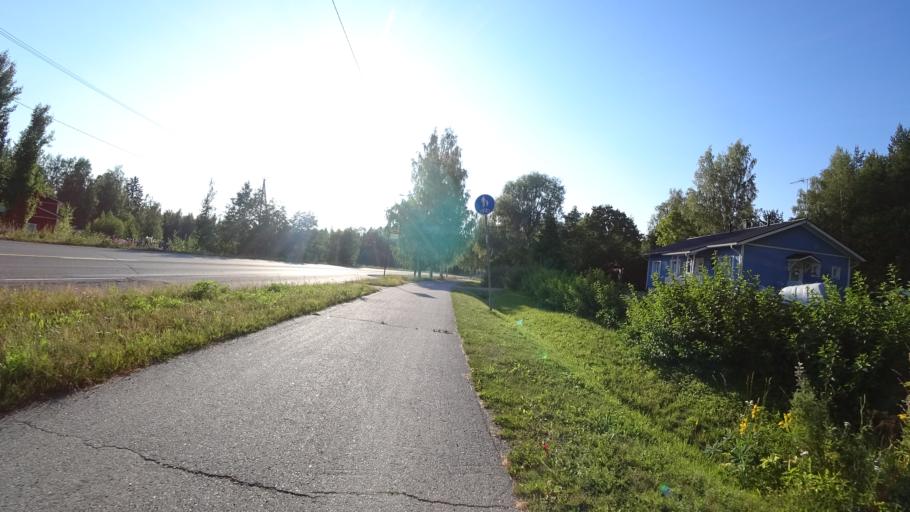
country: FI
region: Pirkanmaa
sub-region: Tampere
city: Nokia
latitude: 61.4682
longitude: 23.3976
